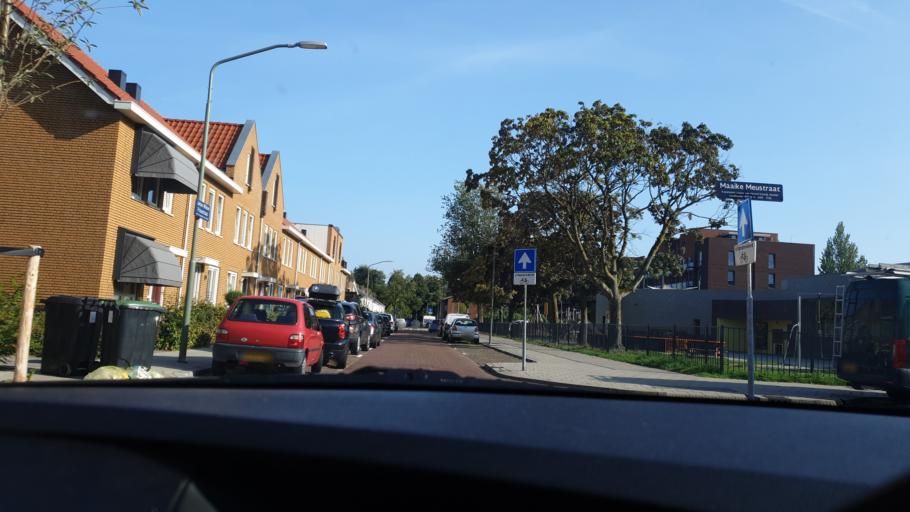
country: NL
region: South Holland
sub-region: Gemeente Dordrecht
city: Dordrecht
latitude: 51.8041
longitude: 4.6705
